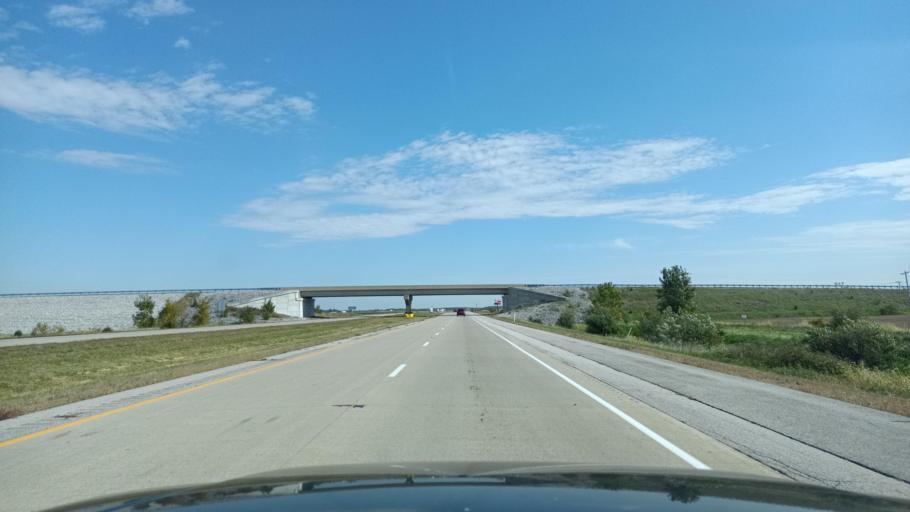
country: US
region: Indiana
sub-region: Allen County
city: Woodburn
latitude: 41.1384
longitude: -84.8656
